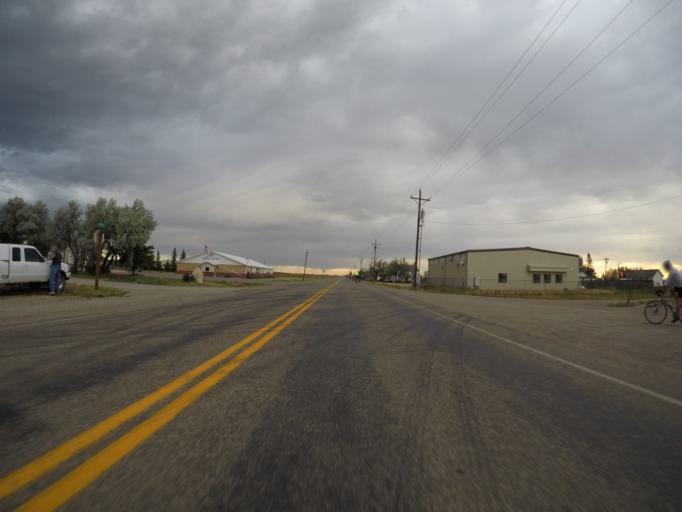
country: US
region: Wyoming
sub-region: Albany County
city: Laramie
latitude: 41.7441
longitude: -105.9755
